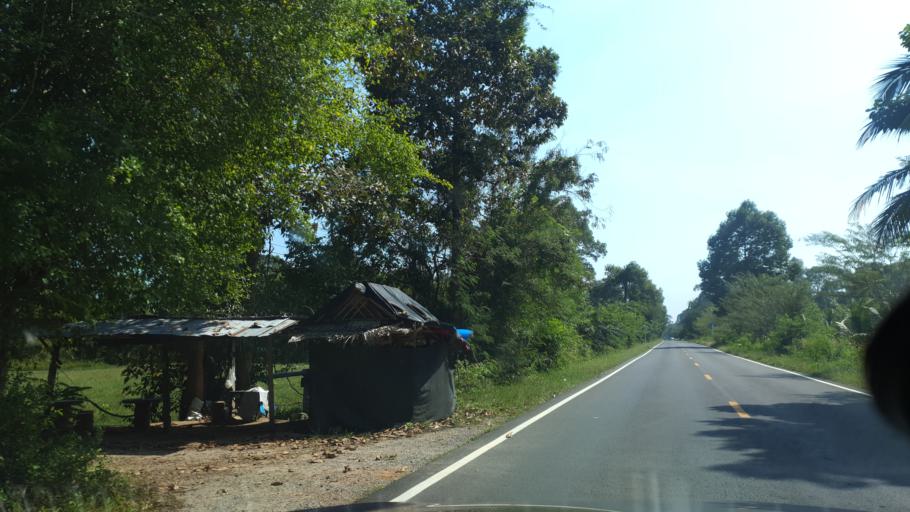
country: TH
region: Surat Thani
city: Tha Chana
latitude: 9.5832
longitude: 99.2026
